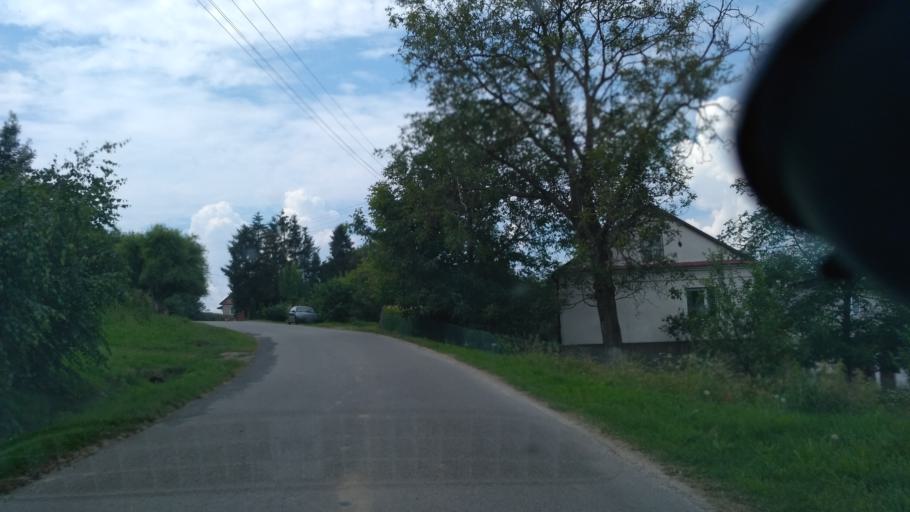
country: PL
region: Subcarpathian Voivodeship
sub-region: Powiat przeworski
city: Lopuszka Wielka
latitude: 49.9162
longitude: 22.4084
